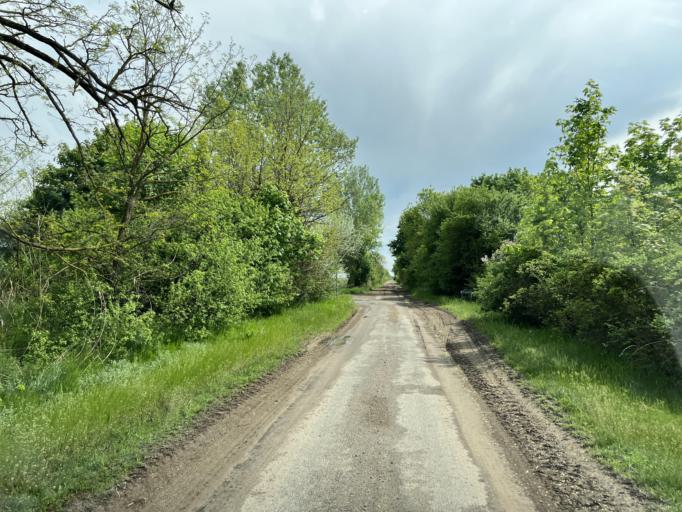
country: HU
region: Pest
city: Nagykoros
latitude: 46.9670
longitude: 19.8203
